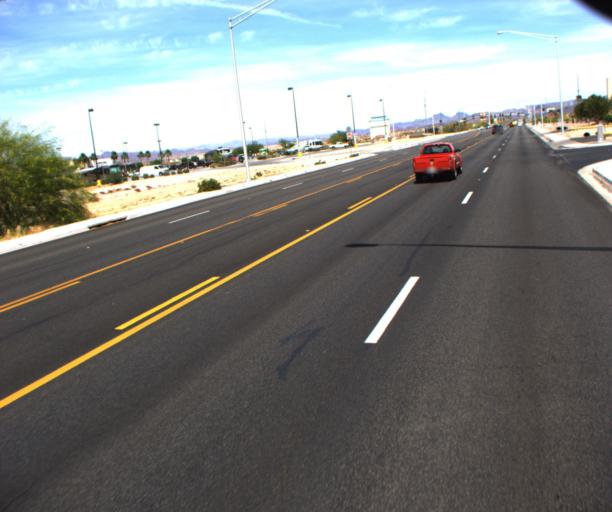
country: US
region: Arizona
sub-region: La Paz County
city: Parker
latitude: 34.1549
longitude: -114.2784
